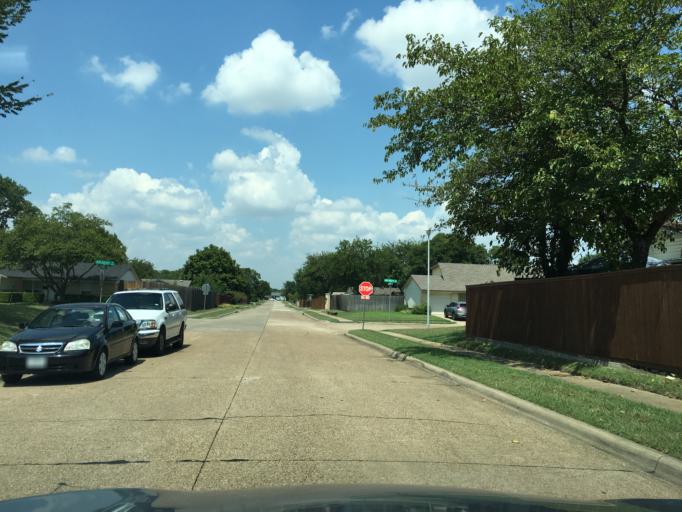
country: US
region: Texas
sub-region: Dallas County
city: Garland
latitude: 32.9394
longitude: -96.6518
